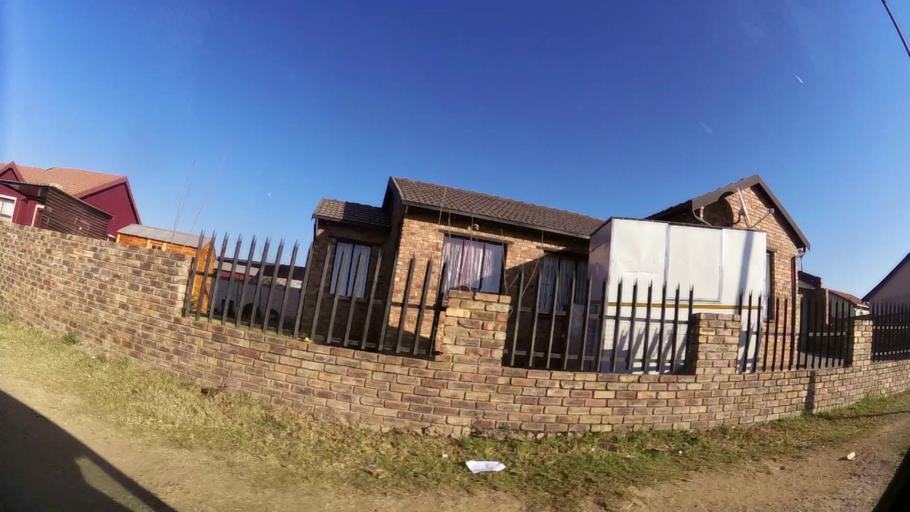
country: ZA
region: Gauteng
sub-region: City of Johannesburg Metropolitan Municipality
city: Midrand
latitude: -25.9119
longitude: 28.1038
